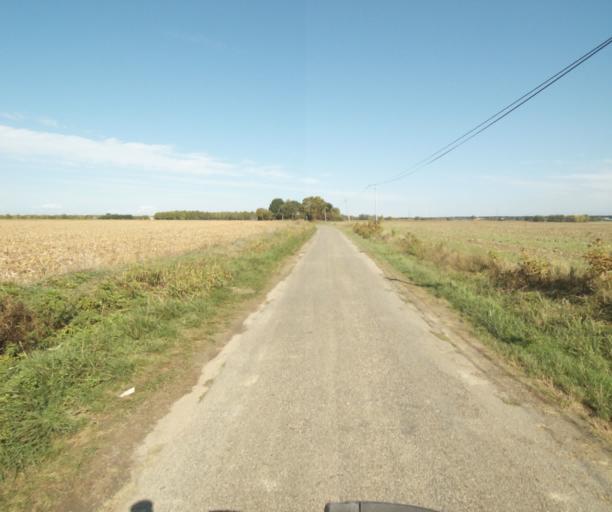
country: FR
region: Midi-Pyrenees
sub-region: Departement du Tarn-et-Garonne
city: Verdun-sur-Garonne
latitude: 43.8735
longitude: 1.2350
